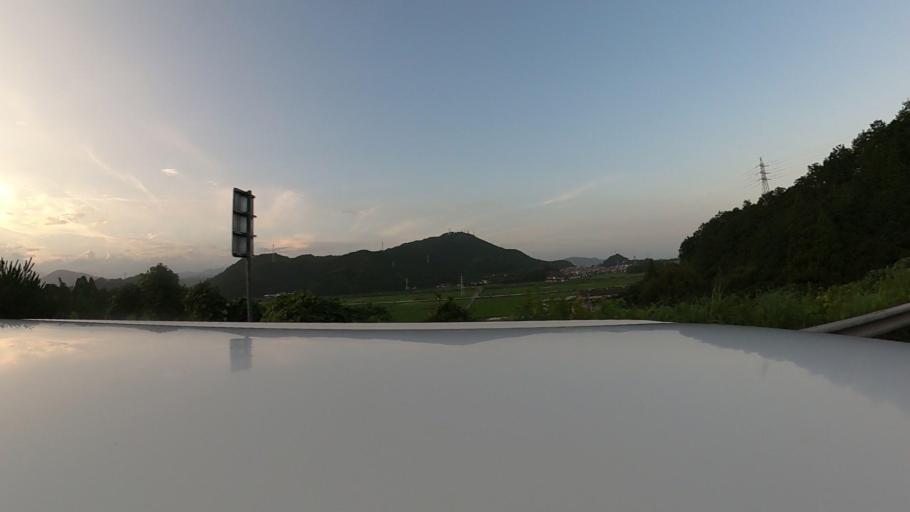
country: JP
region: Miyazaki
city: Nobeoka
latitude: 32.5426
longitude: 131.6521
